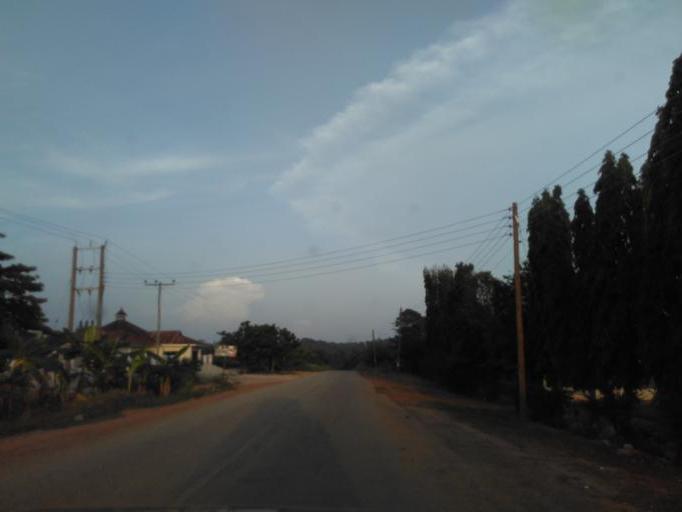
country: GH
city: Bekwai
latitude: 6.5409
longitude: -1.4682
